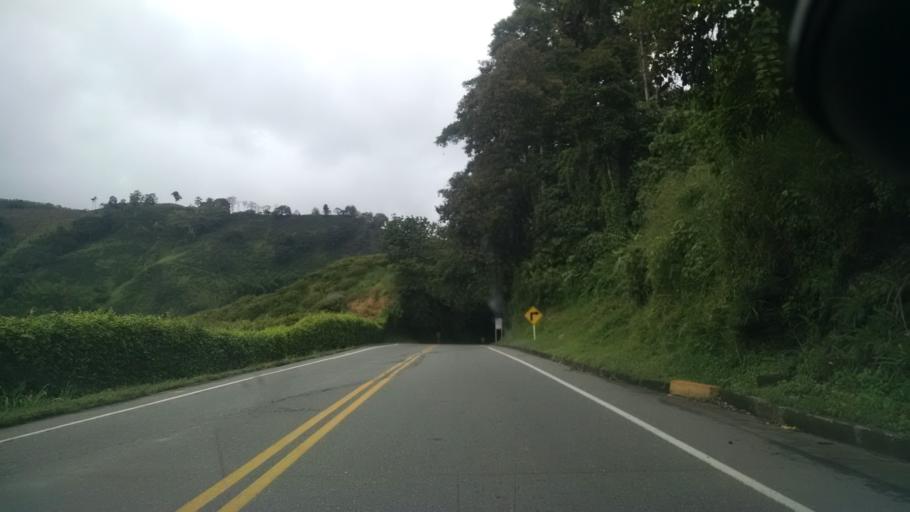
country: CO
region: Caldas
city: Palestina
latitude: 5.0636
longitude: -75.6167
